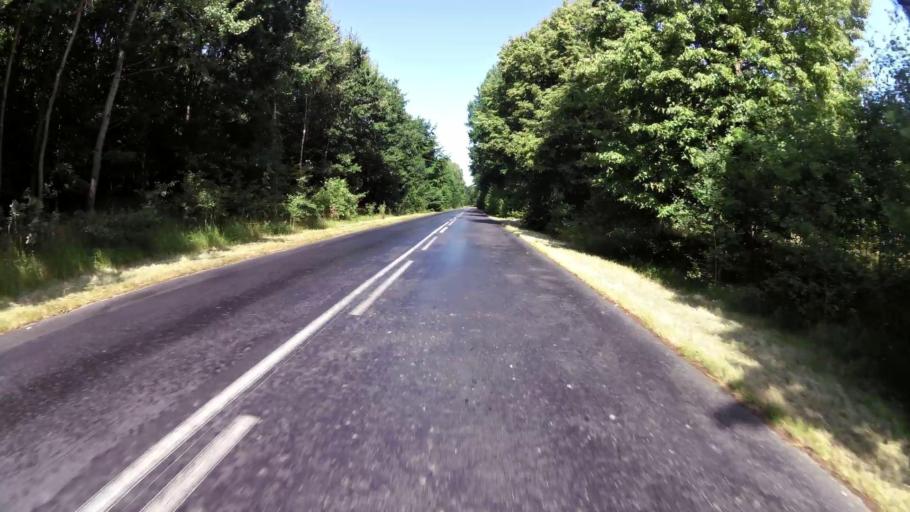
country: PL
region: West Pomeranian Voivodeship
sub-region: Powiat stargardzki
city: Suchan
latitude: 53.3148
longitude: 15.3749
